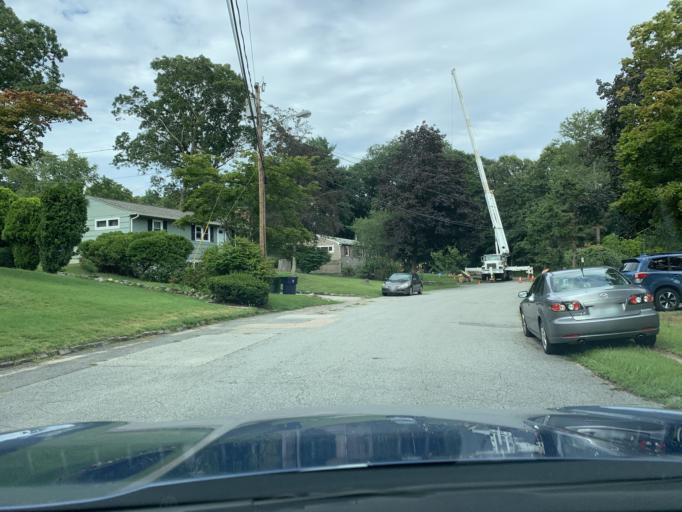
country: US
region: Rhode Island
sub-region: Kent County
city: East Greenwich
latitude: 41.6215
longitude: -71.4546
